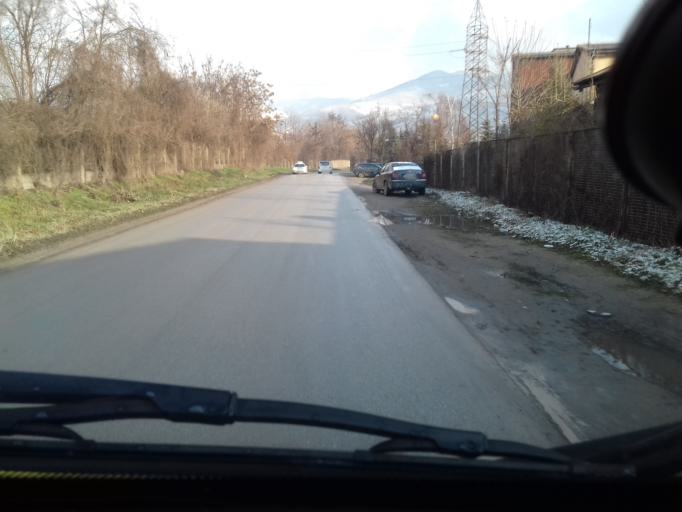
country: BA
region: Federation of Bosnia and Herzegovina
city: Zenica
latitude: 44.2130
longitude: 17.9053
